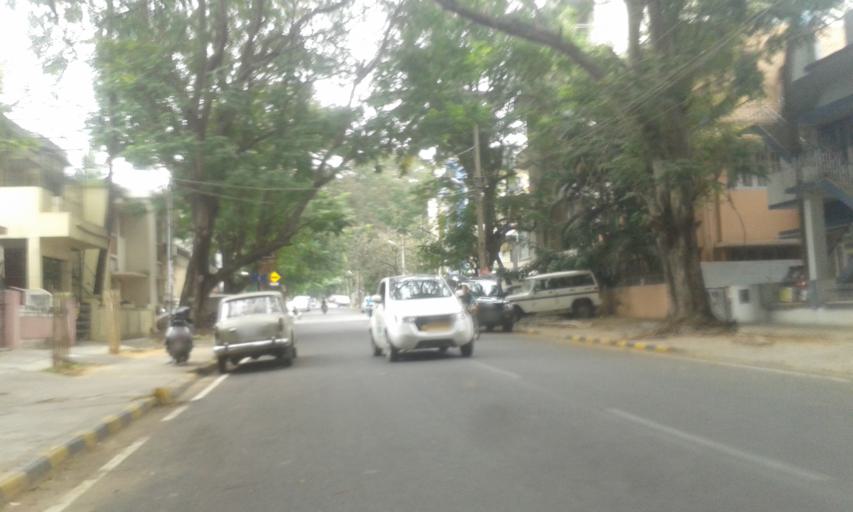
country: IN
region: Karnataka
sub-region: Bangalore Urban
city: Bangalore
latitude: 12.9211
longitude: 77.5914
